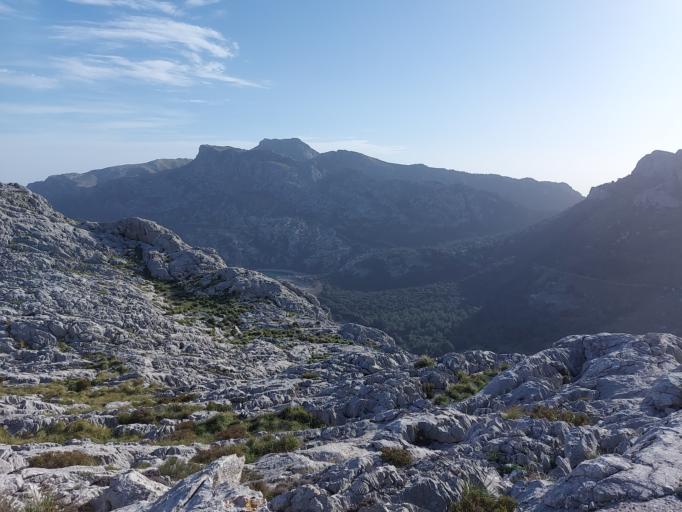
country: ES
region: Balearic Islands
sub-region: Illes Balears
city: Fornalutx
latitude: 39.7971
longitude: 2.7999
